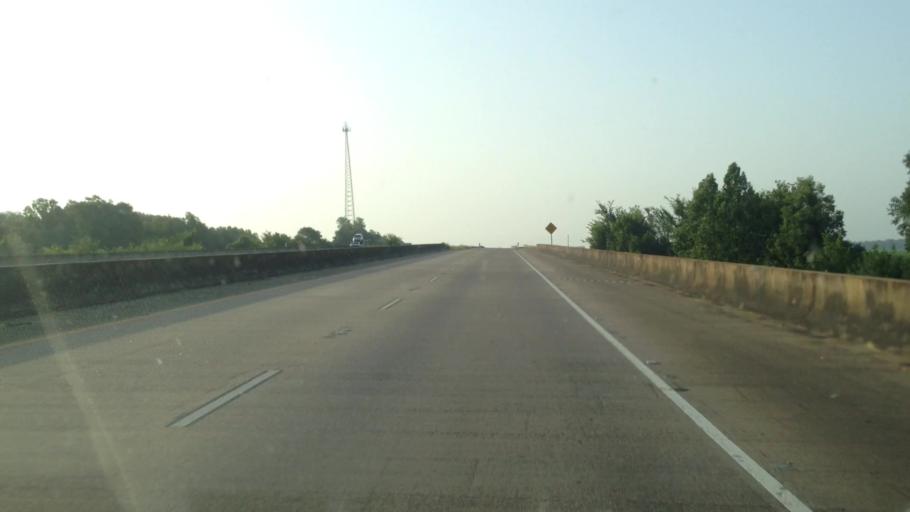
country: US
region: Louisiana
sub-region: Rapides Parish
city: Boyce
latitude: 31.3945
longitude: -92.6960
